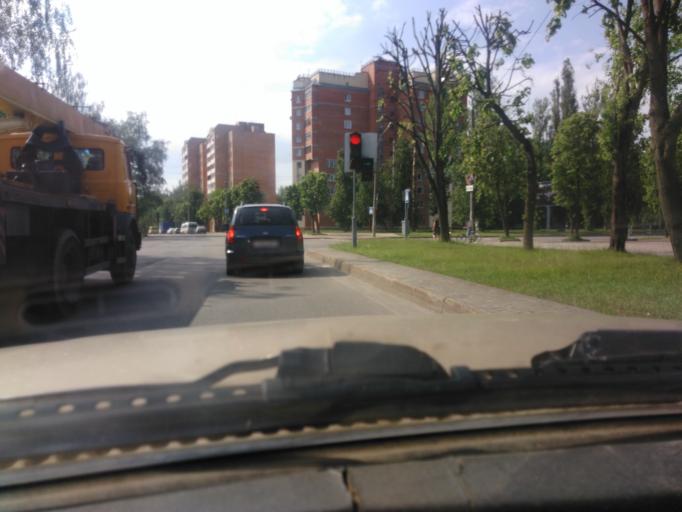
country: BY
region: Mogilev
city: Mahilyow
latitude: 53.9268
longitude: 30.3623
